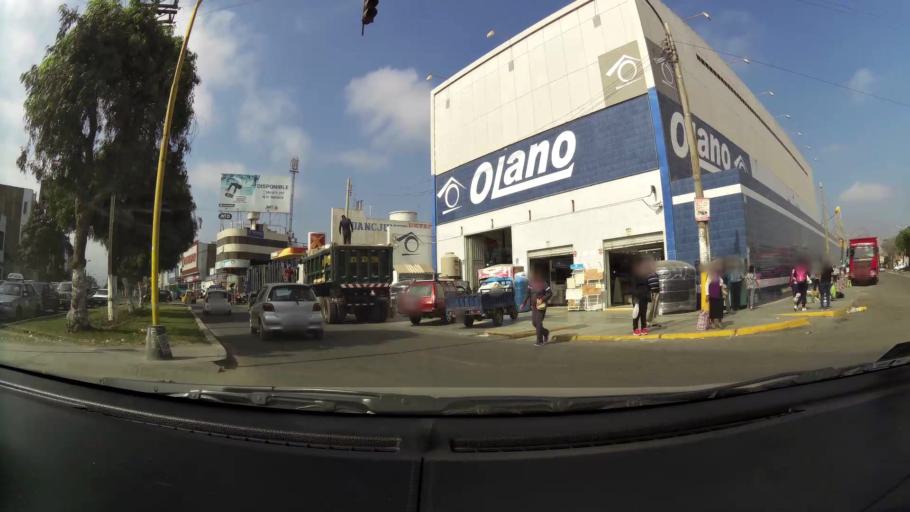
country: PE
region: La Libertad
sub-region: Provincia de Trujillo
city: Trujillo
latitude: -8.1148
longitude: -79.0151
